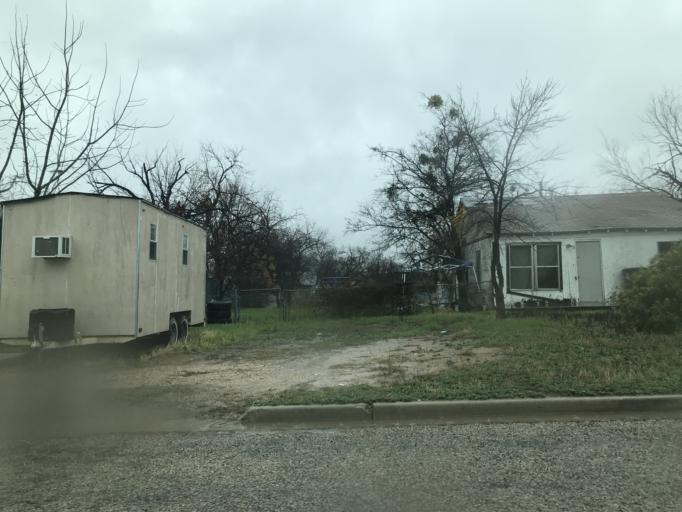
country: US
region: Texas
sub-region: Tom Green County
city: San Angelo
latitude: 31.4626
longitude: -100.4192
